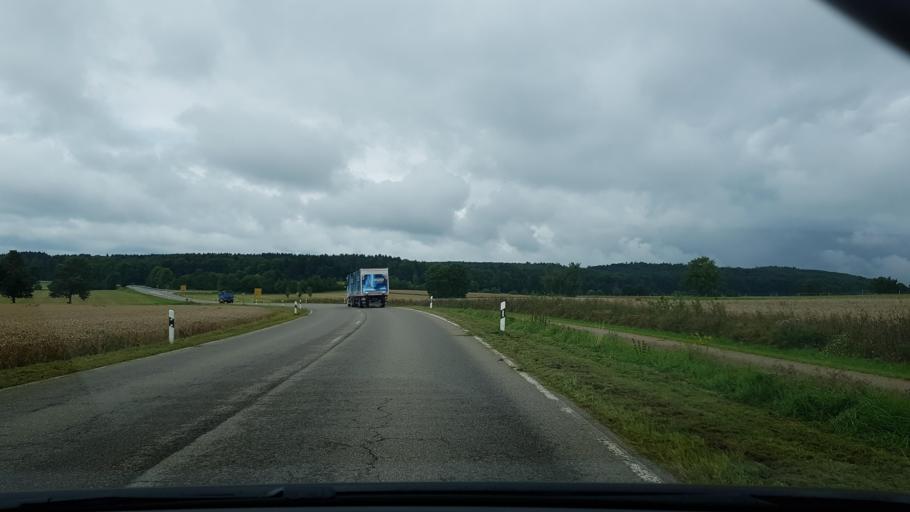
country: DE
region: Baden-Wuerttemberg
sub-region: Tuebingen Region
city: Laichingen
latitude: 48.4636
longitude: 9.6750
